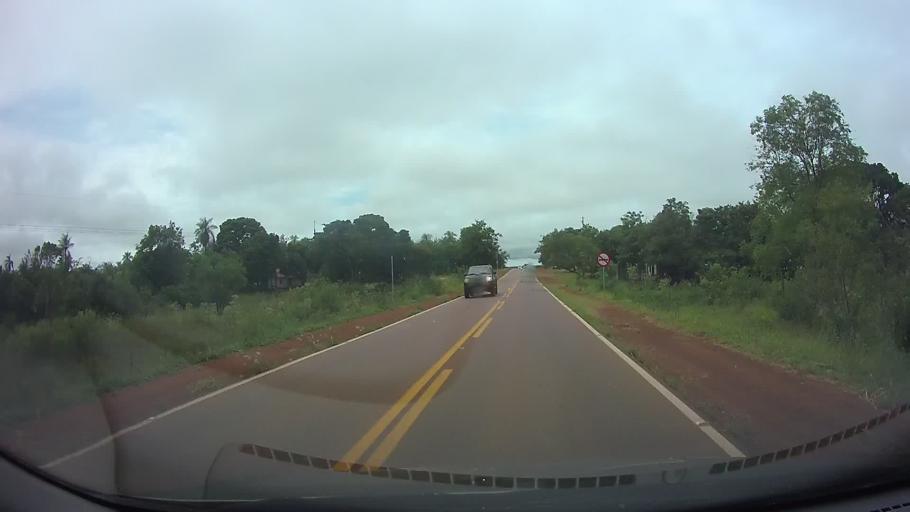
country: PY
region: Paraguari
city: Acahay
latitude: -25.8682
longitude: -57.1270
